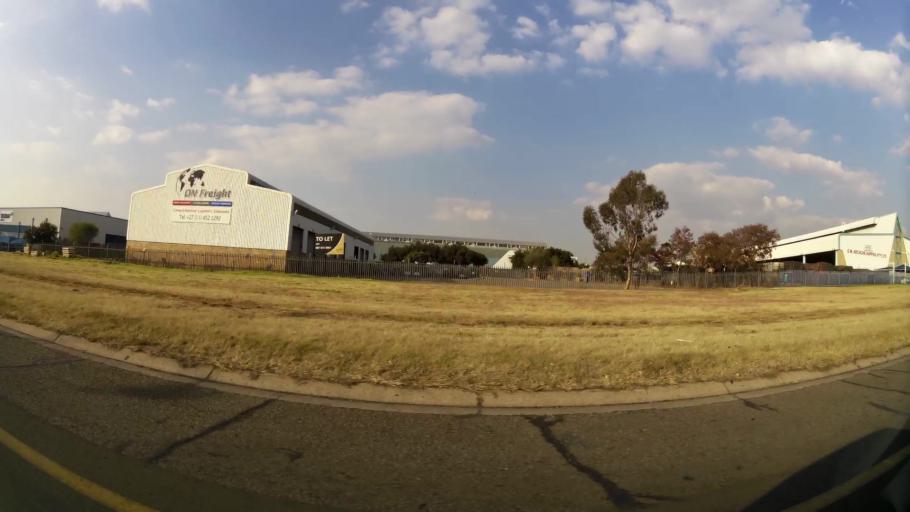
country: ZA
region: Gauteng
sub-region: City of Johannesburg Metropolitan Municipality
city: Modderfontein
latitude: -26.1237
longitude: 28.2014
